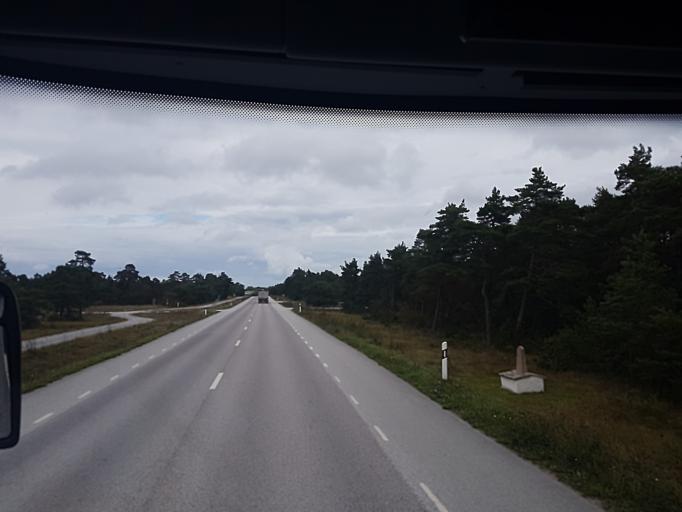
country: SE
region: Gotland
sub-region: Gotland
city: Vibble
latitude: 57.5633
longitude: 18.2048
